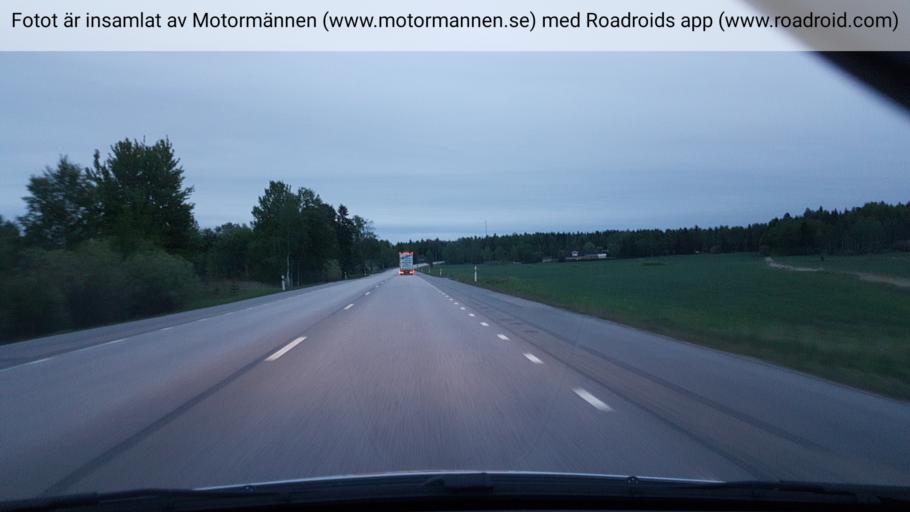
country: SE
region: Uppsala
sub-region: Heby Kommun
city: Heby
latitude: 59.9368
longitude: 16.7430
